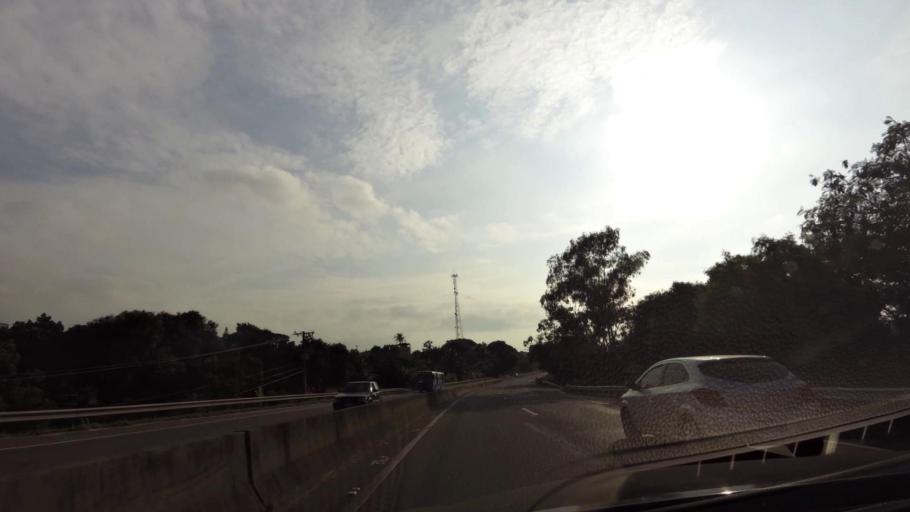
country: BR
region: Espirito Santo
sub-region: Viana
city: Viana
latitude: -20.5002
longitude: -40.3630
